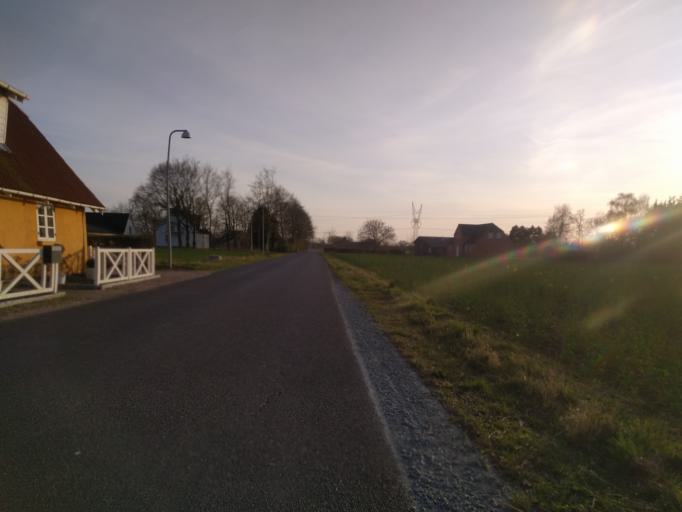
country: DK
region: South Denmark
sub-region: Odense Kommune
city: Bullerup
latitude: 55.4293
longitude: 10.5046
